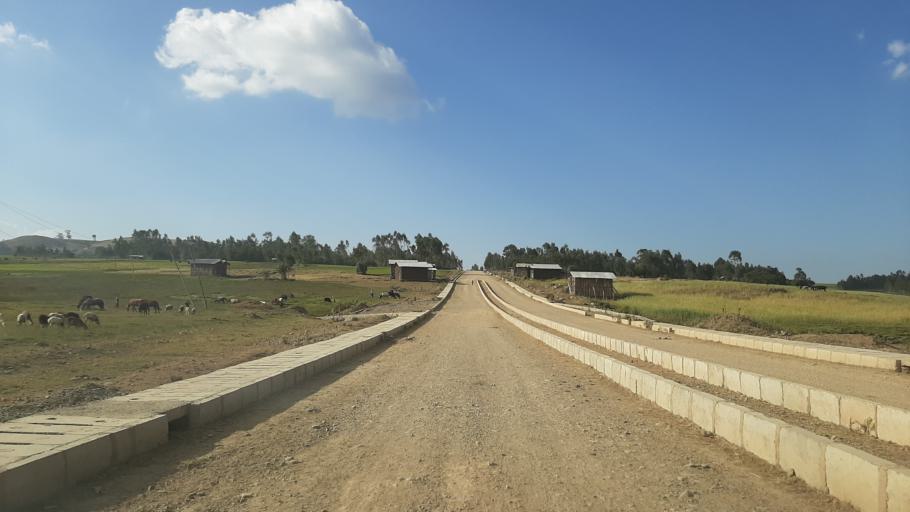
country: ET
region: Amhara
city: Dabat
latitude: 12.9947
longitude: 37.7643
